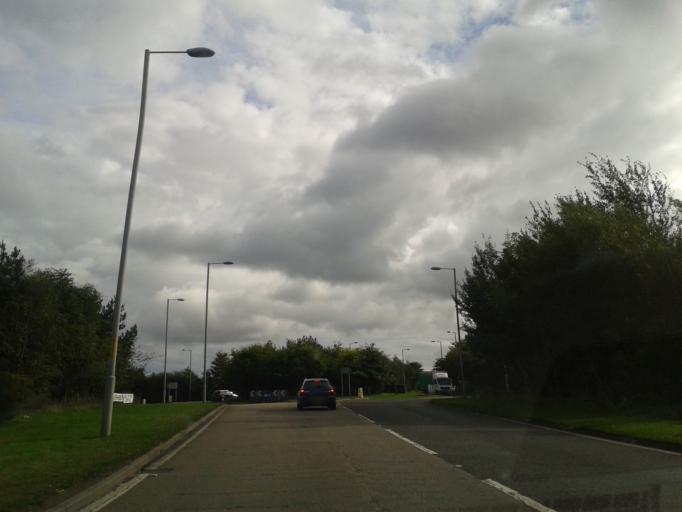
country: GB
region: Scotland
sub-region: Moray
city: Lhanbryd
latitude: 57.6359
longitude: -3.2347
